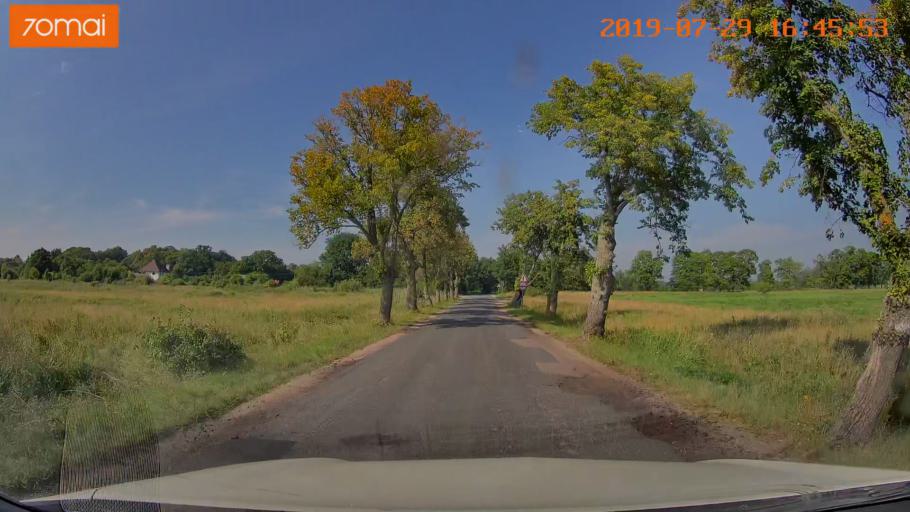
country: RU
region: Kaliningrad
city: Primorsk
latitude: 54.7692
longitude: 20.0796
